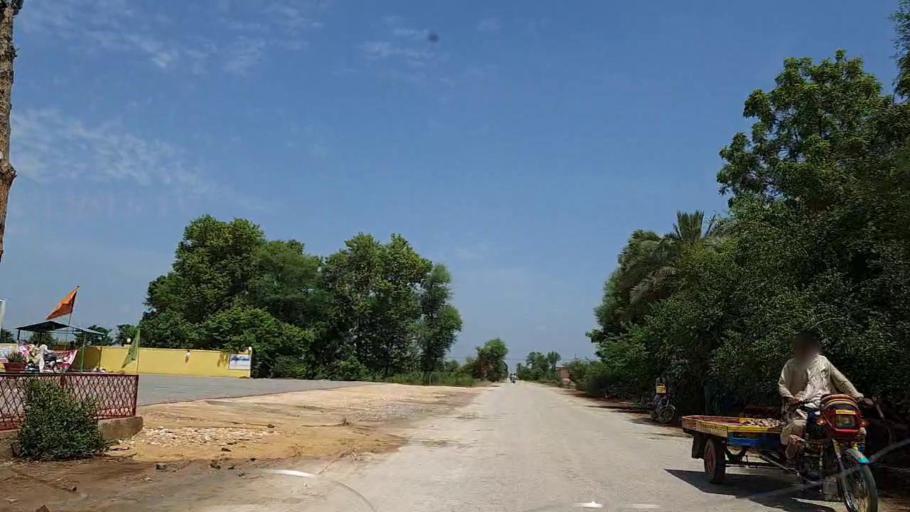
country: PK
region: Sindh
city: Naushahro Firoz
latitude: 26.8331
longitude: 68.1329
